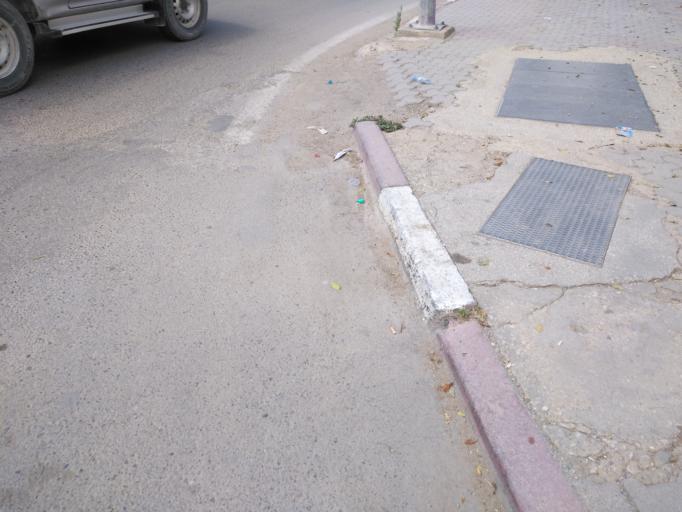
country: TN
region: Silyanah
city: Siliana
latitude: 36.0849
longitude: 9.3696
